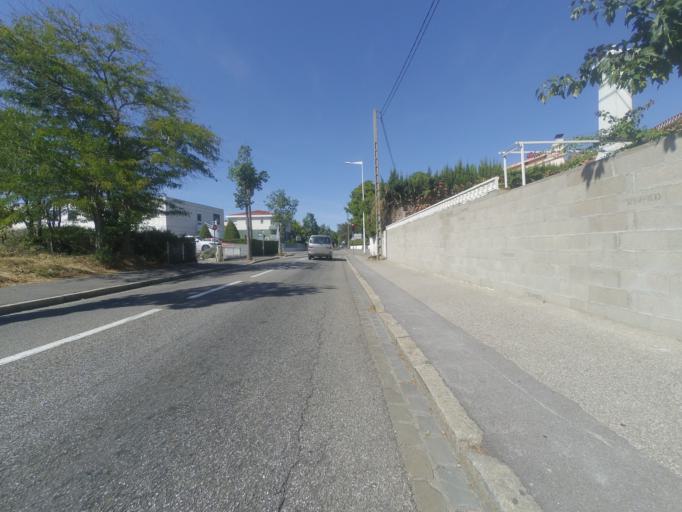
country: FR
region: Languedoc-Roussillon
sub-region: Departement des Pyrenees-Orientales
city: Perpignan
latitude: 42.6890
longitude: 2.9069
